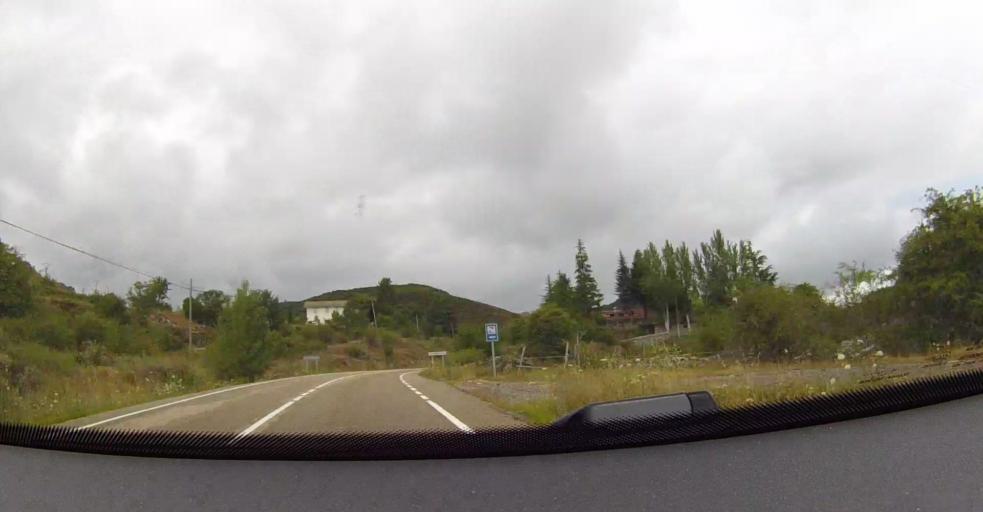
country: ES
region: Castille and Leon
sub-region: Provincia de Leon
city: Bonar
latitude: 42.9043
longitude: -5.3126
